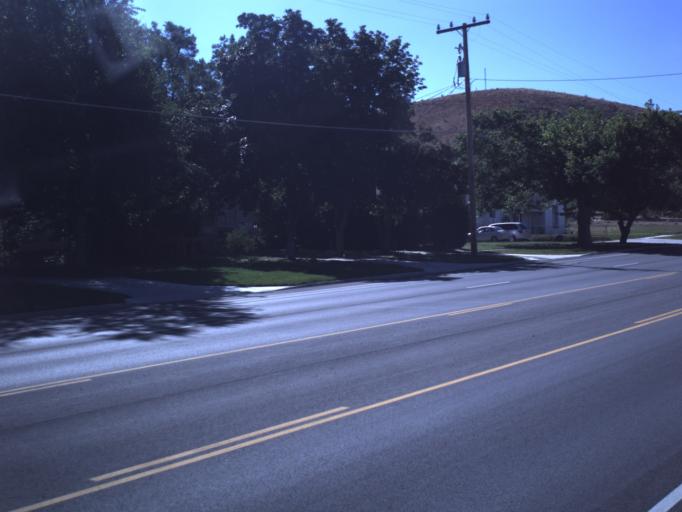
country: US
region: Utah
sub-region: Tooele County
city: Tooele
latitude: 40.5243
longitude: -112.2988
